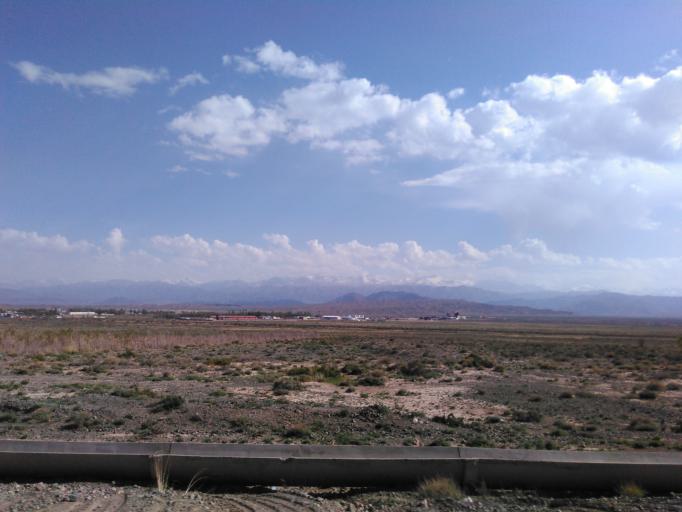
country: KG
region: Ysyk-Koel
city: Balykchy
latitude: 42.4562
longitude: 76.1418
